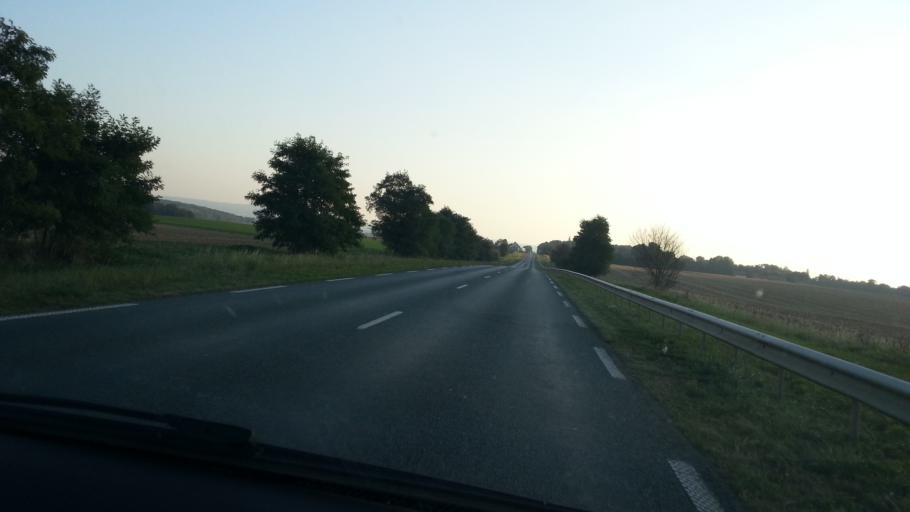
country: FR
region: Picardie
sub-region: Departement de l'Oise
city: Grandfresnoy
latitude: 49.3924
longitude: 2.6228
